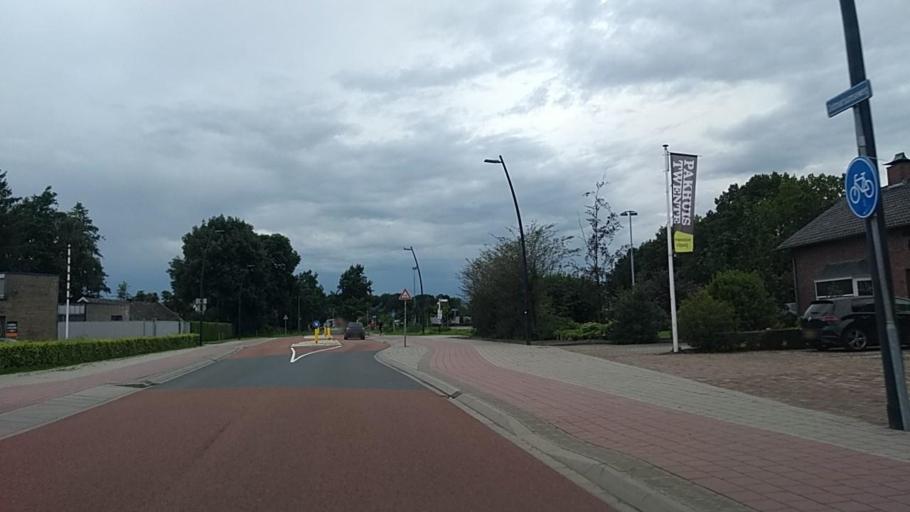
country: NL
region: Overijssel
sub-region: Gemeente Tubbergen
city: Tubbergen
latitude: 52.3736
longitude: 6.7618
